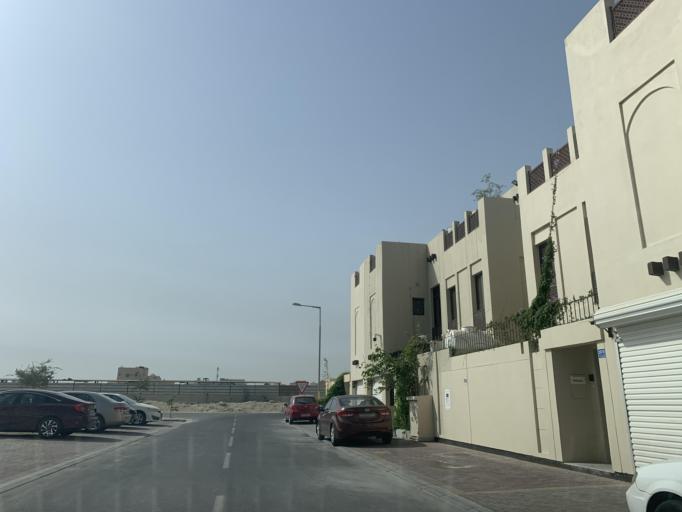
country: BH
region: Northern
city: Madinat `Isa
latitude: 26.1851
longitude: 50.5630
